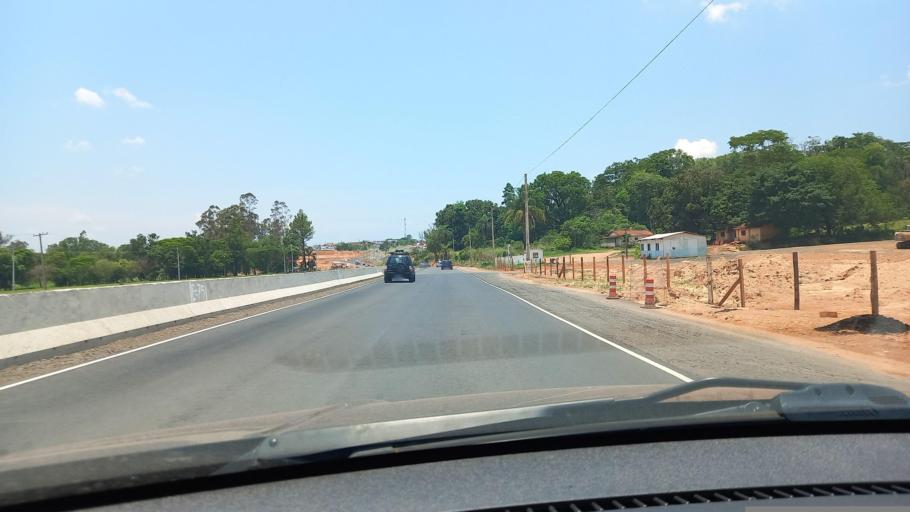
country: BR
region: Sao Paulo
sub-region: Itapira
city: Itapira
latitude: -22.4018
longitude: -46.8465
